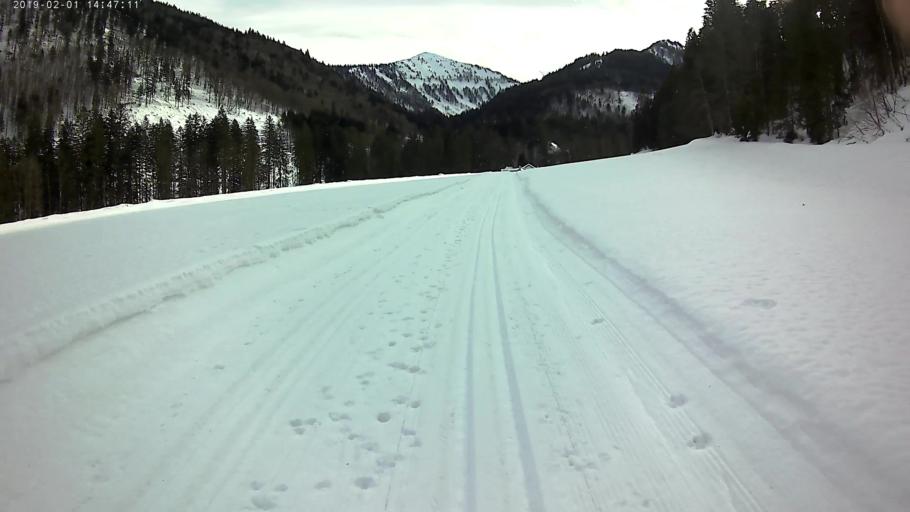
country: AT
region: Salzburg
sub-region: Politischer Bezirk Salzburg-Umgebung
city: Hintersee
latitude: 47.7116
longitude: 13.2853
